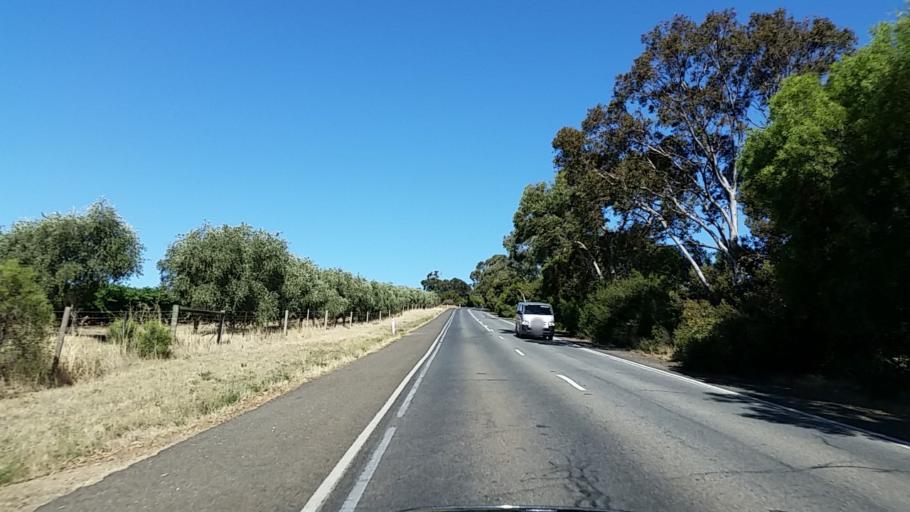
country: AU
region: South Australia
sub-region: Salisbury
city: Elizabeth
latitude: -34.7082
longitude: 138.7164
